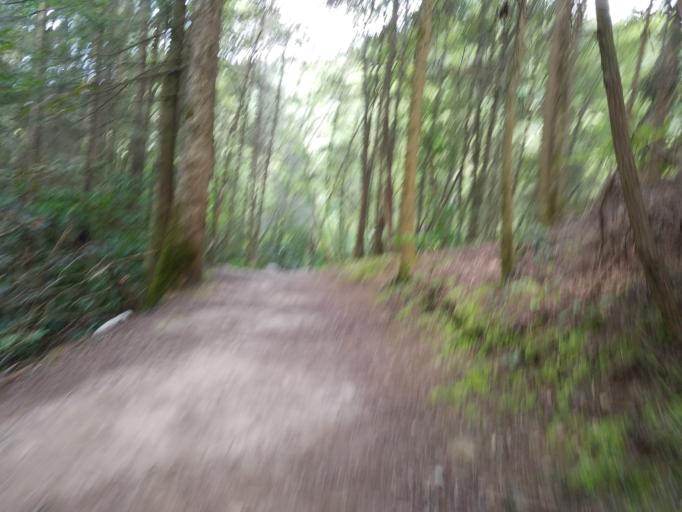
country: US
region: Georgia
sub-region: Fannin County
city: Blue Ridge
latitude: 34.7844
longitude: -84.3027
